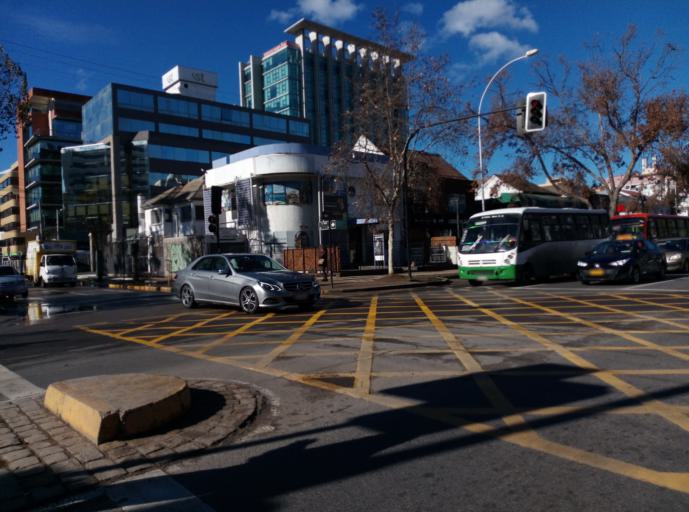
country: CL
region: Valparaiso
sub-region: Provincia de Valparaiso
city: Vina del Mar
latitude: -33.0102
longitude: -71.5491
